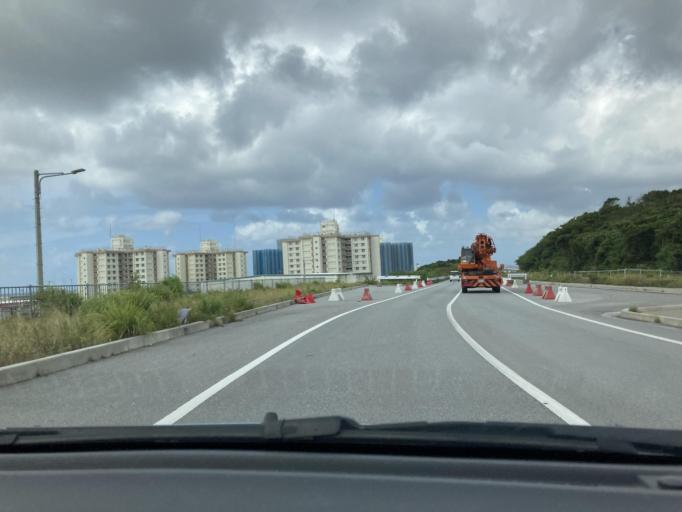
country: JP
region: Okinawa
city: Ginowan
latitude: 26.2639
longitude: 127.7086
